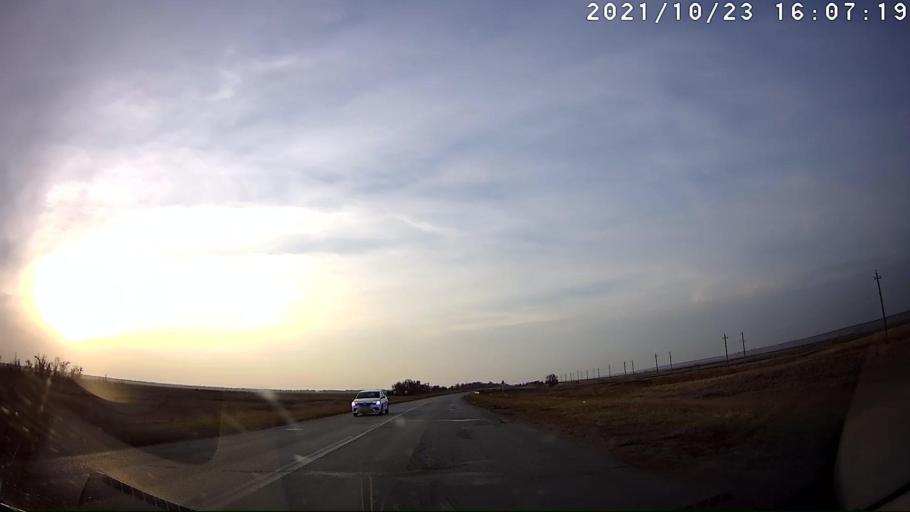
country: RU
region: Volgograd
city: Kotel'nikovo
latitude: 47.9326
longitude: 43.7397
